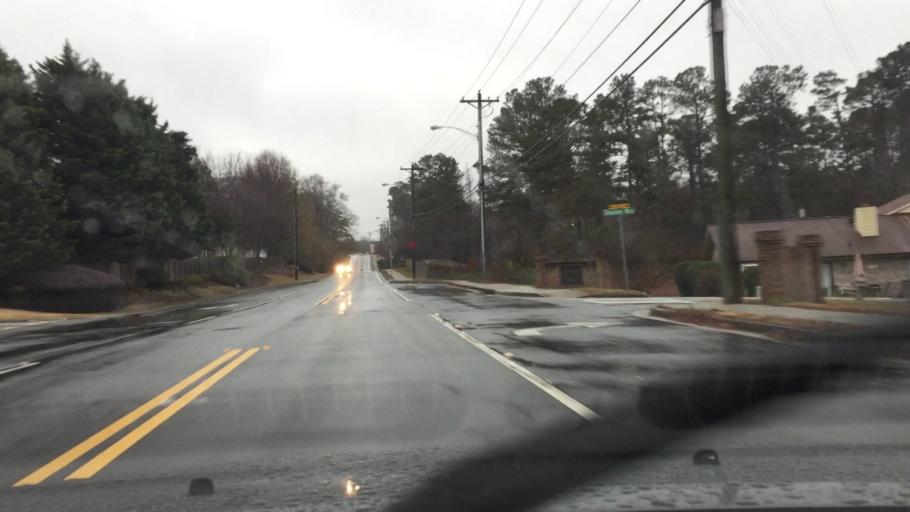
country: US
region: Georgia
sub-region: Cobb County
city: Fair Oaks
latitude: 33.9174
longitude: -84.5766
